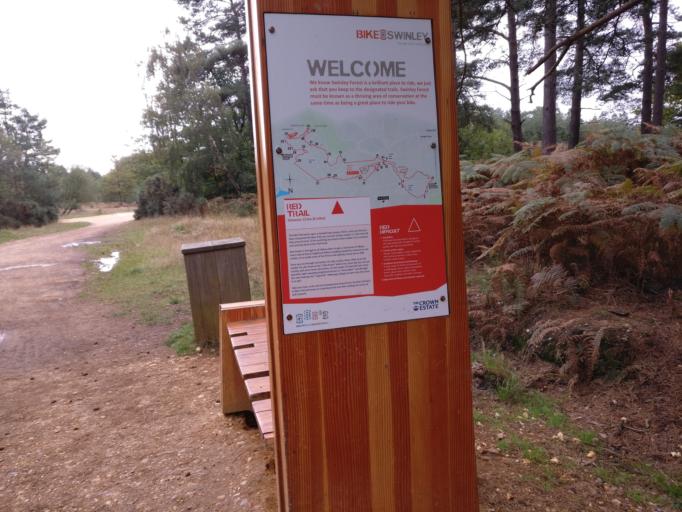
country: GB
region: England
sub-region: Surrey
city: Camberley
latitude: 51.3692
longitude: -0.7441
